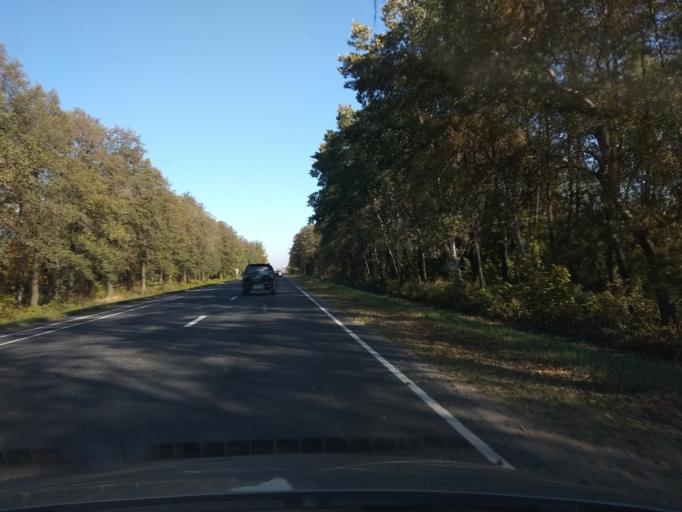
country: BY
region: Brest
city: Kobryn
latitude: 52.1670
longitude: 24.3153
